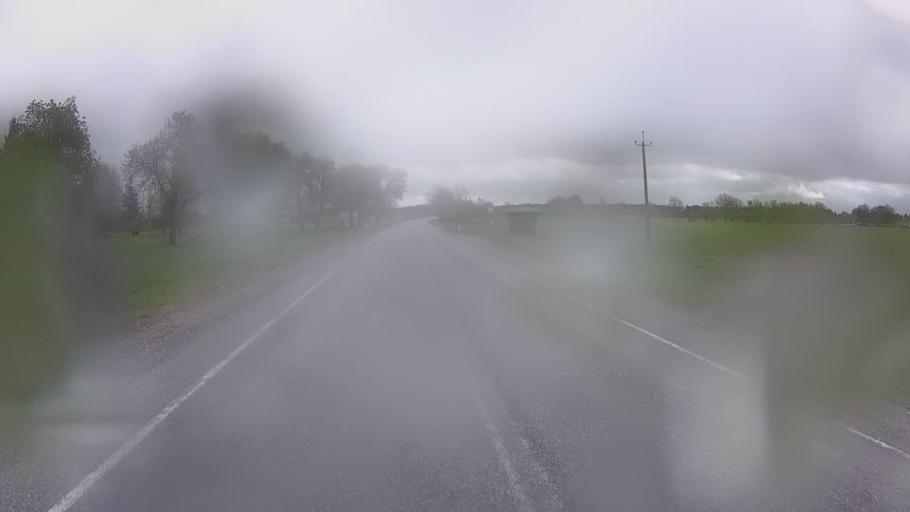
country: EE
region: Hiiumaa
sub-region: Kaerdla linn
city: Kardla
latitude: 58.8352
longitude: 22.7981
